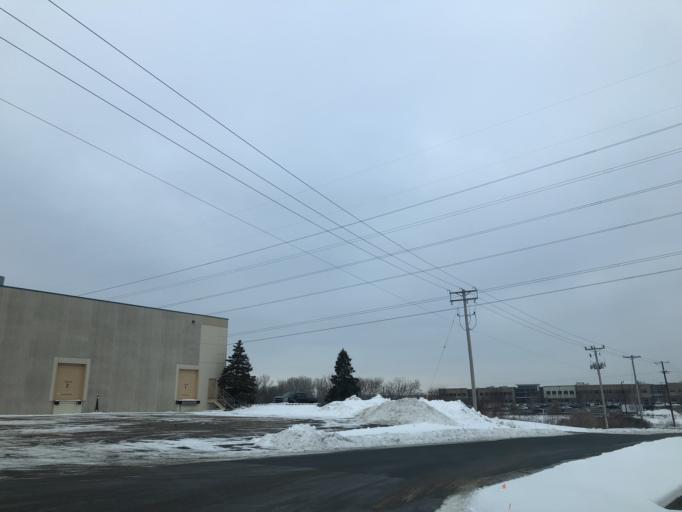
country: US
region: Minnesota
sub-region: Ramsey County
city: New Brighton
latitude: 45.0718
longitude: -93.1835
